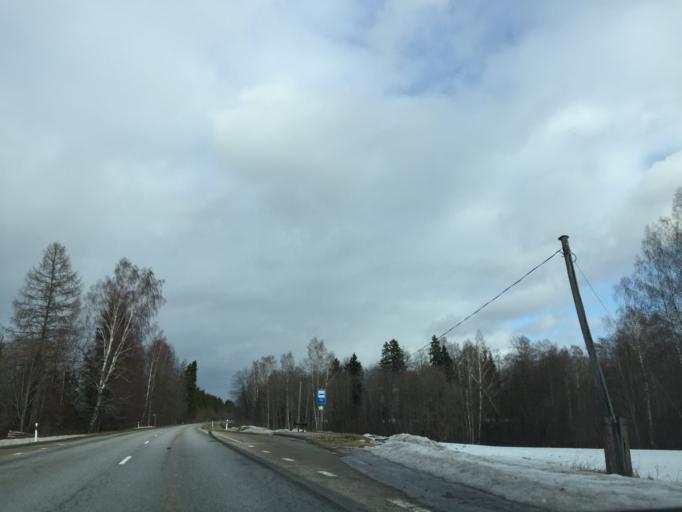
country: LV
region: Aloja
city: Staicele
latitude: 57.8858
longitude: 24.6077
